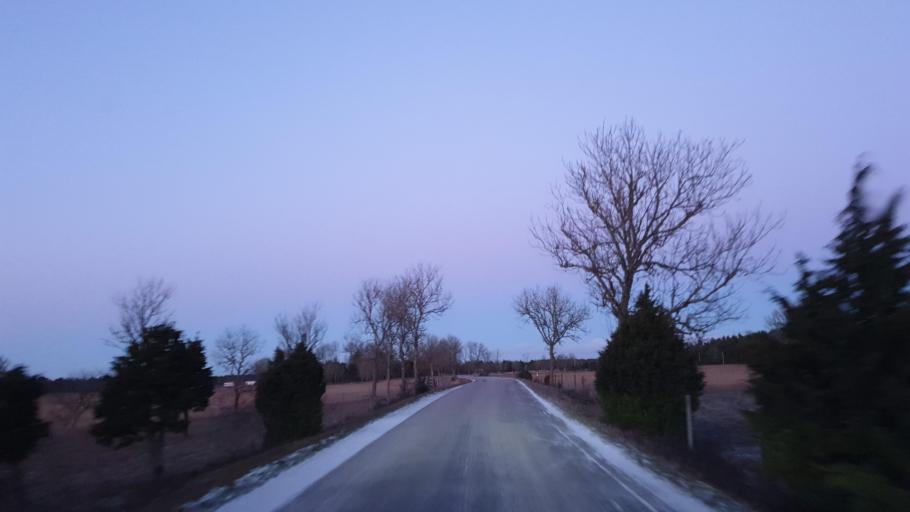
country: SE
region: Gotland
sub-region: Gotland
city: Slite
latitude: 57.4195
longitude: 18.8201
